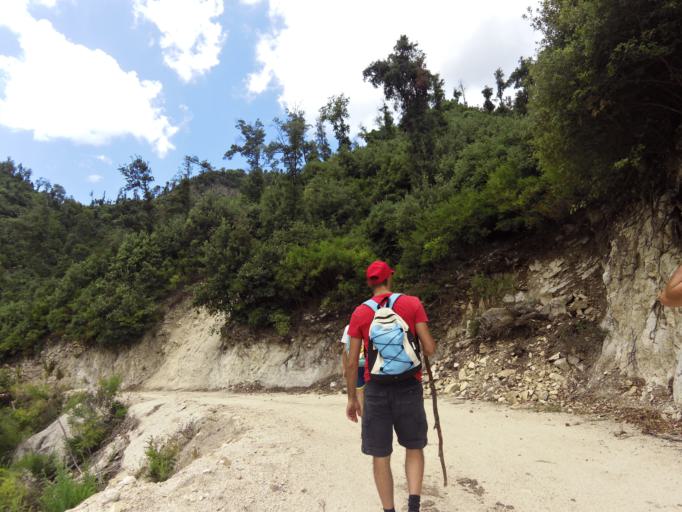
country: IT
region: Calabria
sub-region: Provincia di Reggio Calabria
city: Bivongi
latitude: 38.5062
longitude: 16.3955
